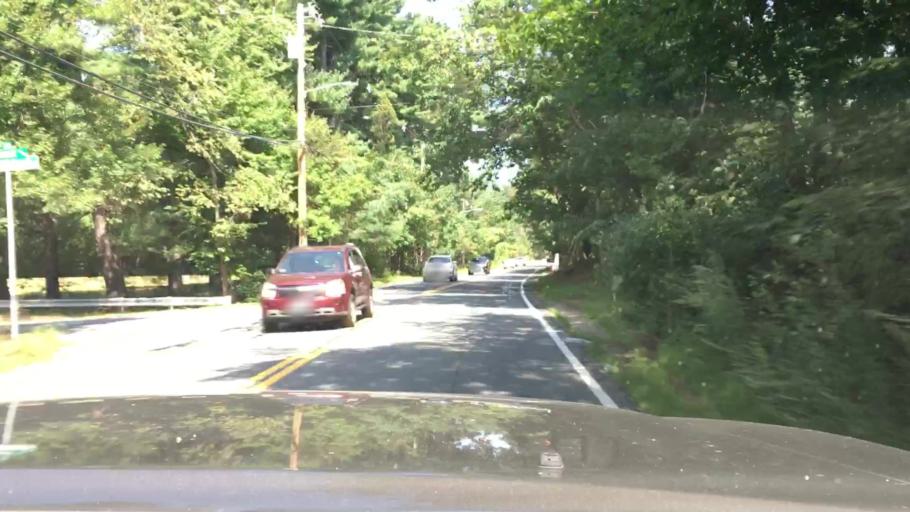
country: US
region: Massachusetts
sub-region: Middlesex County
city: Cochituate
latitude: 42.3283
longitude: -71.3319
